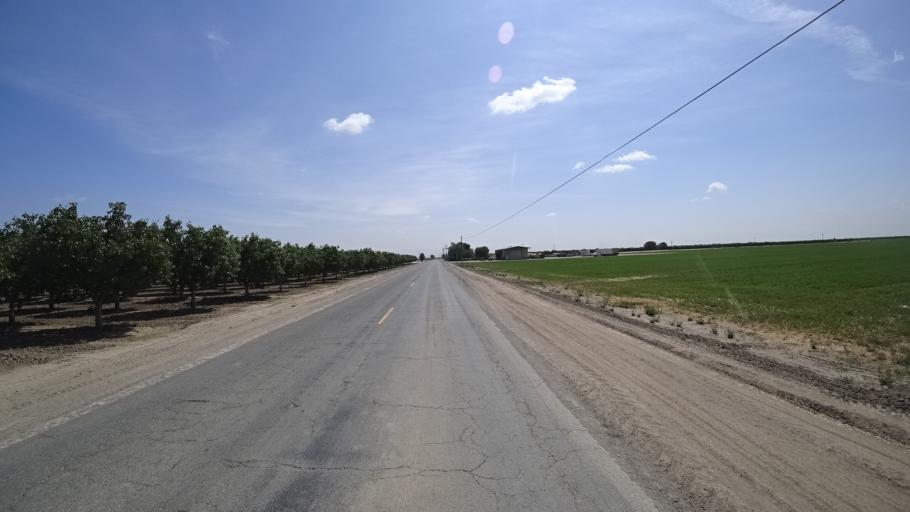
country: US
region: California
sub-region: Kings County
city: Home Garden
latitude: 36.2696
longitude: -119.5423
